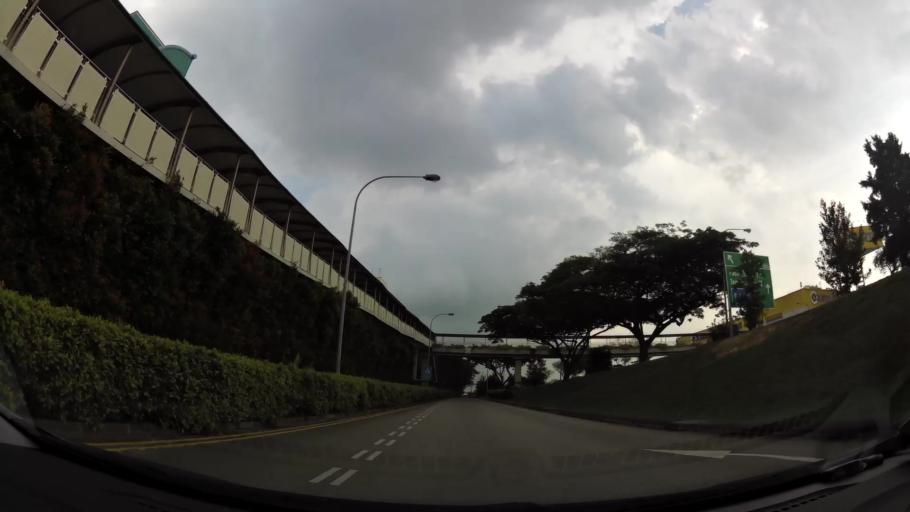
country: MY
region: Johor
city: Kampung Pasir Gudang Baru
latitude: 1.3754
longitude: 103.9337
